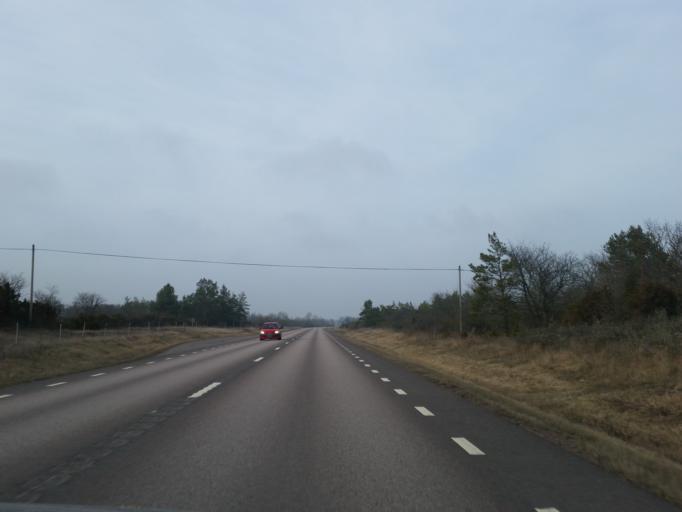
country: SE
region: Kalmar
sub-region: Borgholms Kommun
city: Borgholm
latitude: 57.0877
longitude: 16.9231
